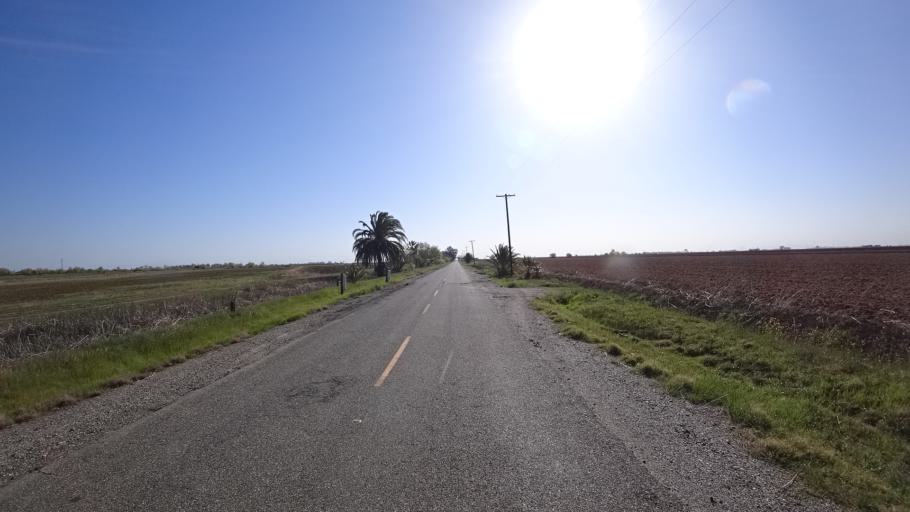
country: US
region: California
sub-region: Glenn County
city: Willows
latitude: 39.5096
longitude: -122.1823
